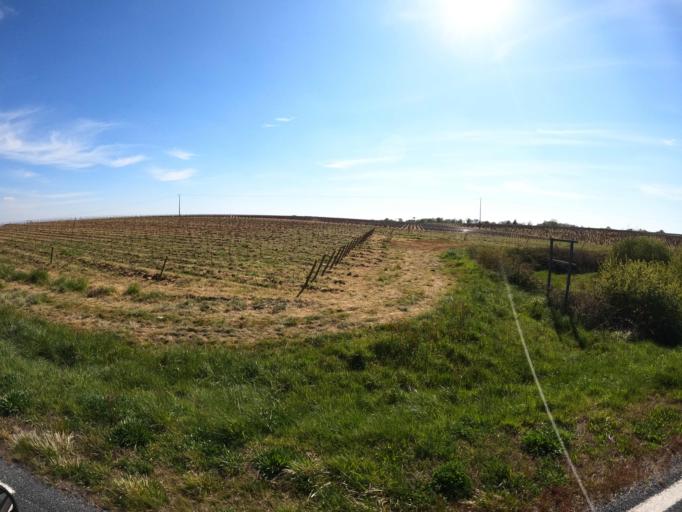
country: FR
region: Pays de la Loire
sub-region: Departement de la Loire-Atlantique
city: Gorges
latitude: 47.1104
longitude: -1.2836
